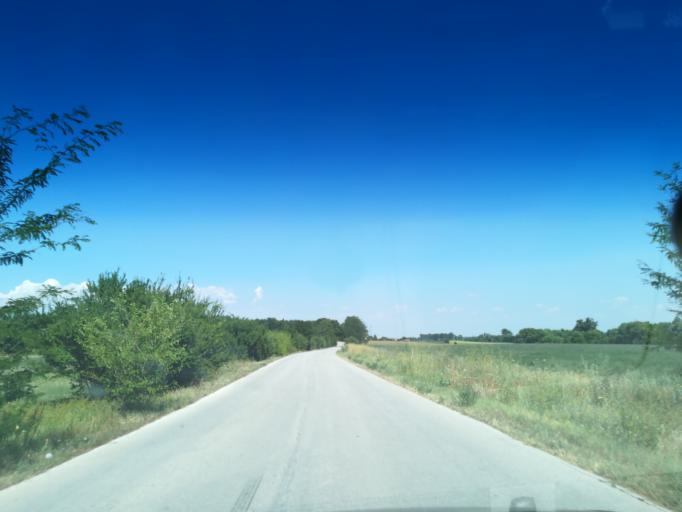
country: BG
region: Plovdiv
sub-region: Obshtina Sadovo
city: Sadovo
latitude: 42.0195
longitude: 25.0850
